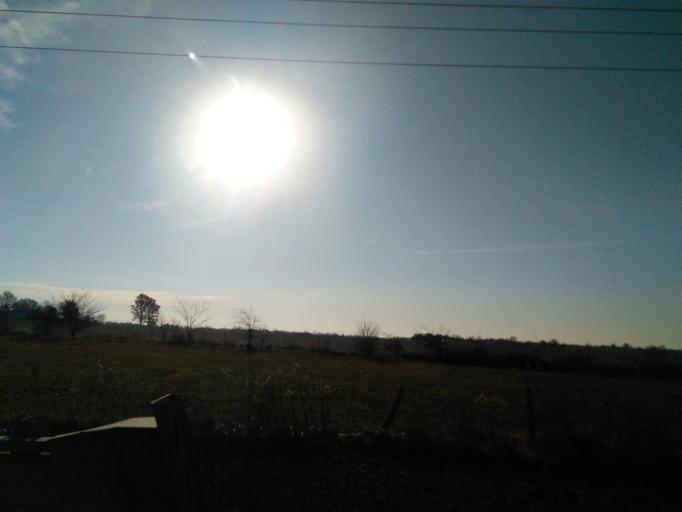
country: US
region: Illinois
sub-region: Bond County
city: Greenville
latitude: 38.8756
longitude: -89.3991
